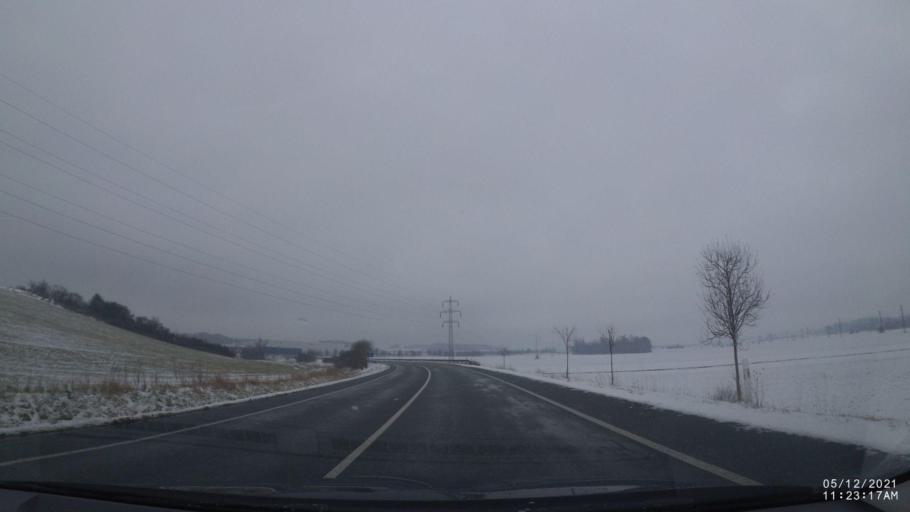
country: CZ
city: Solnice
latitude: 50.1945
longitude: 16.2410
